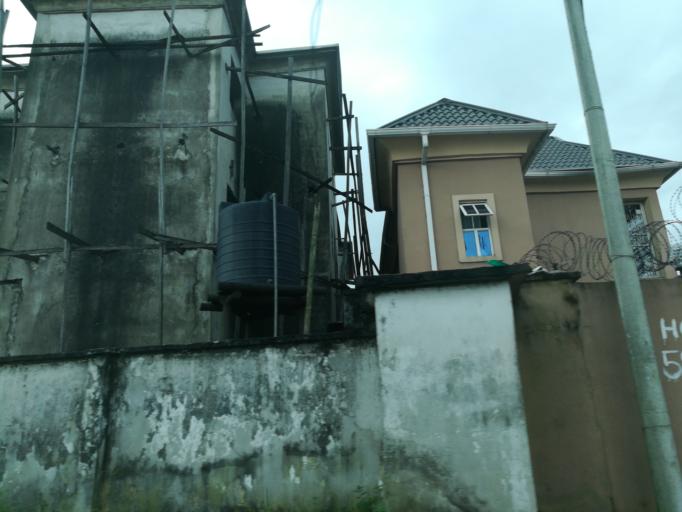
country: NG
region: Rivers
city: Port Harcourt
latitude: 4.8378
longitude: 7.0324
